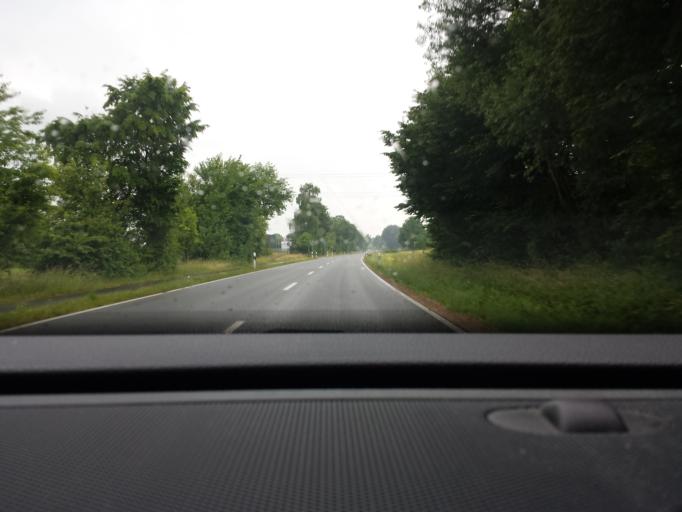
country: DE
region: North Rhine-Westphalia
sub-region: Regierungsbezirk Munster
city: Ahaus
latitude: 52.0730
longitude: 6.9695
